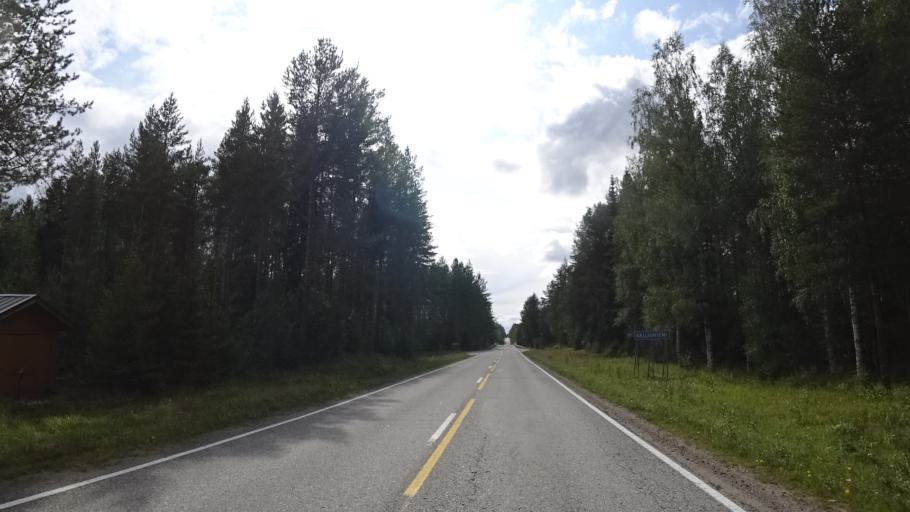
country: FI
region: North Karelia
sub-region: Joensuu
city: Ilomantsi
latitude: 62.7599
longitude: 31.0153
